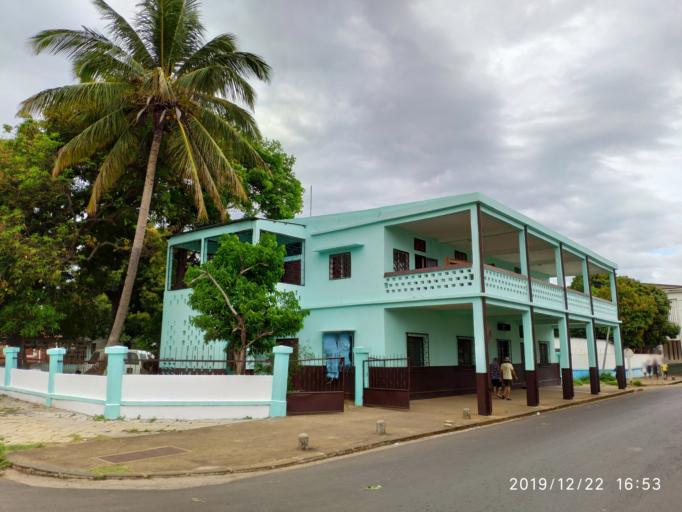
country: MG
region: Diana
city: Antsiranana
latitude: -12.2704
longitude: 49.2932
